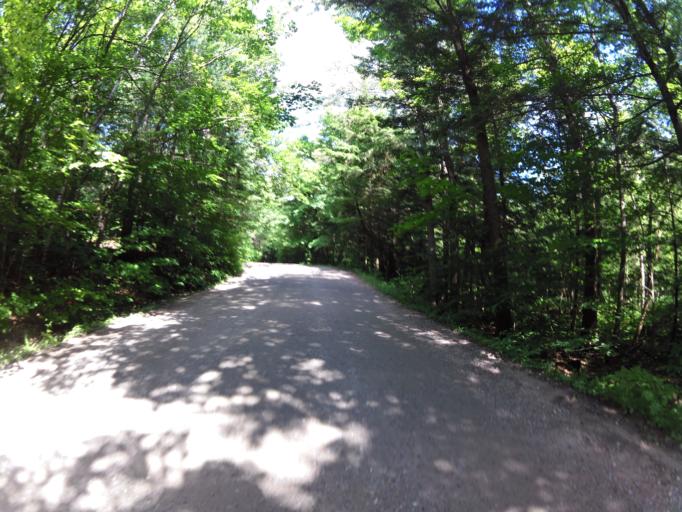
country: CA
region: Quebec
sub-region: Outaouais
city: Wakefield
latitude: 45.5993
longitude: -76.0035
